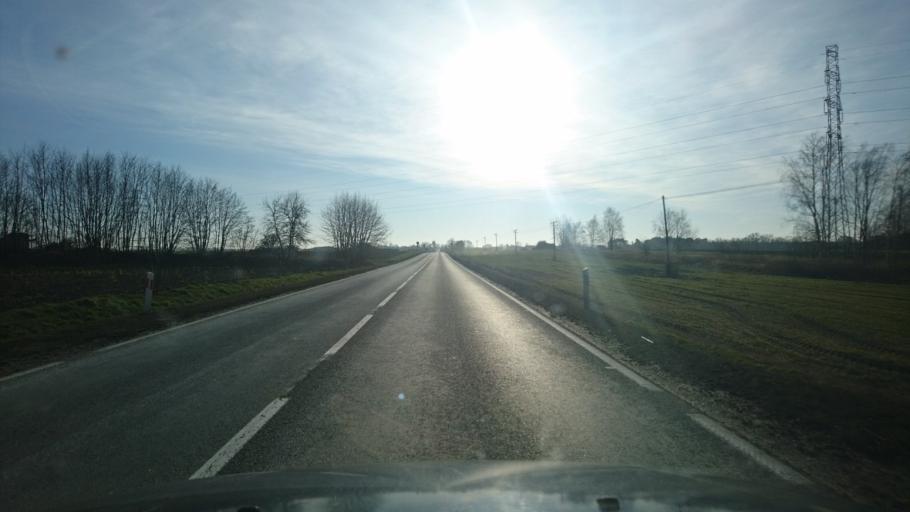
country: PL
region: Opole Voivodeship
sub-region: Powiat oleski
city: Dalachow
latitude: 51.0608
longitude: 18.5998
